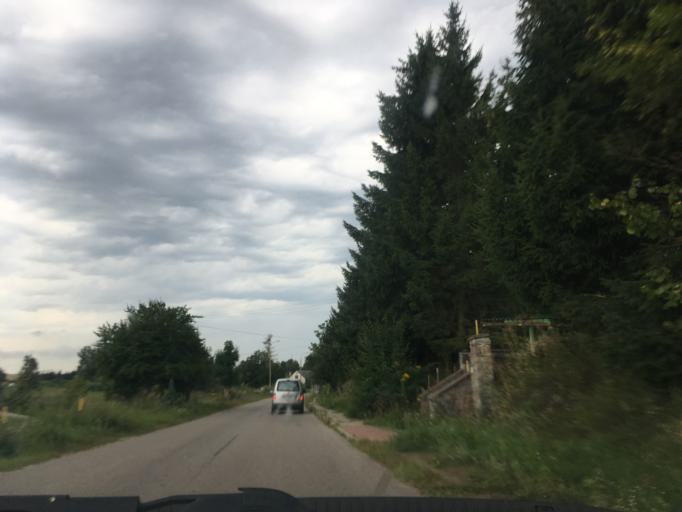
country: PL
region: Warmian-Masurian Voivodeship
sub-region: Powiat gizycki
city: Gizycko
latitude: 54.0886
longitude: 21.7870
